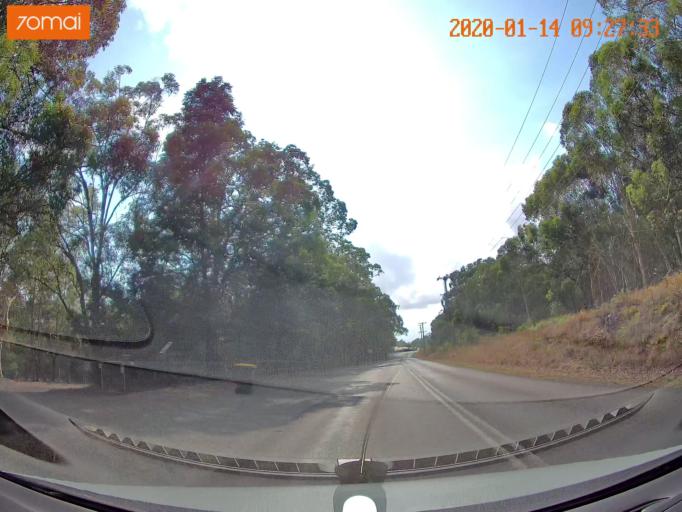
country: AU
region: New South Wales
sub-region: Lake Macquarie Shire
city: Dora Creek
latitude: -33.1200
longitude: 151.5258
